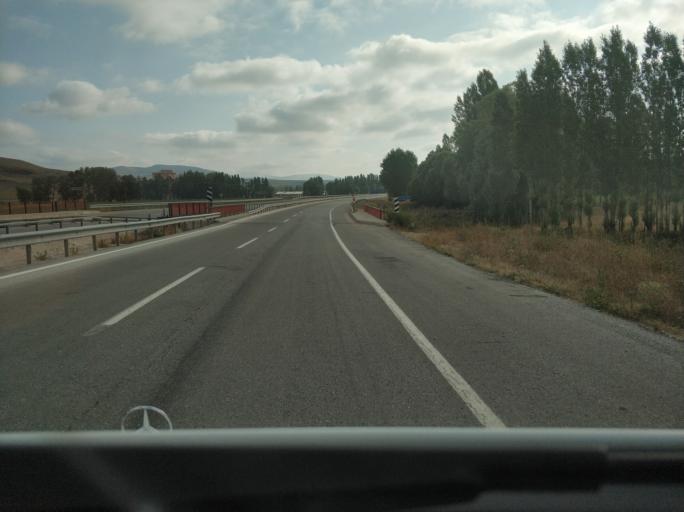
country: TR
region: Sivas
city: Yildizeli
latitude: 39.8671
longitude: 36.5800
